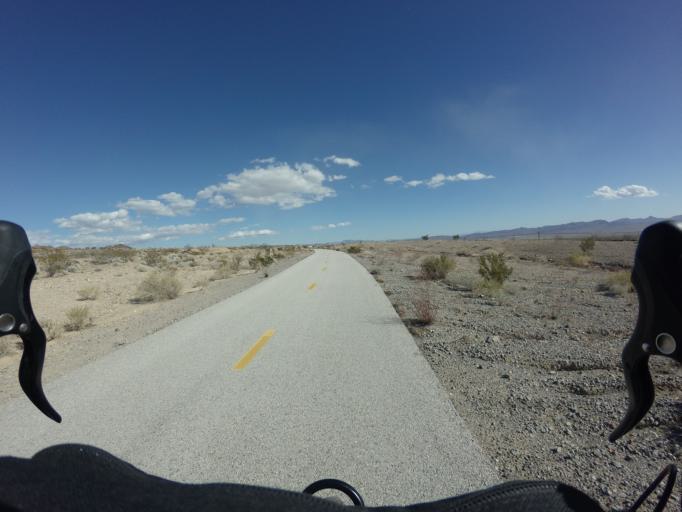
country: US
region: Nevada
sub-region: Clark County
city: Boulder City
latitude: 35.9684
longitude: -114.8884
